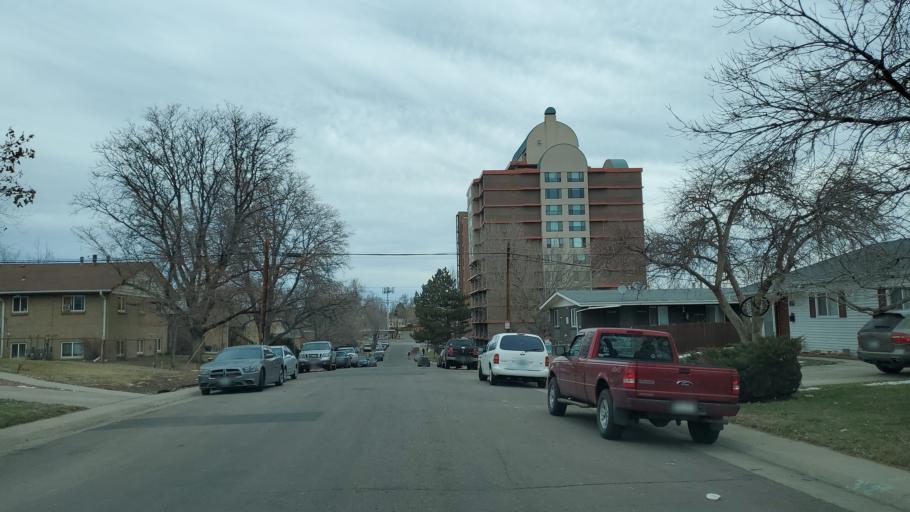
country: US
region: Colorado
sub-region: Arapahoe County
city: Sheridan
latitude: 39.6945
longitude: -105.0088
